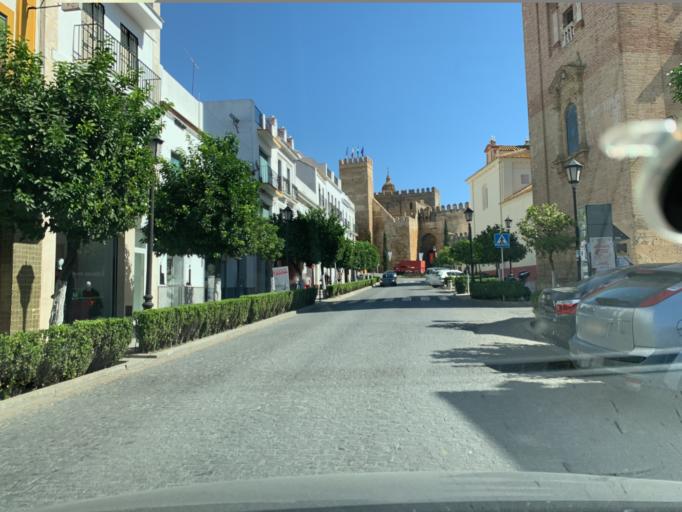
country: ES
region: Andalusia
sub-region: Provincia de Sevilla
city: Carmona
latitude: 37.4711
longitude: -5.6428
